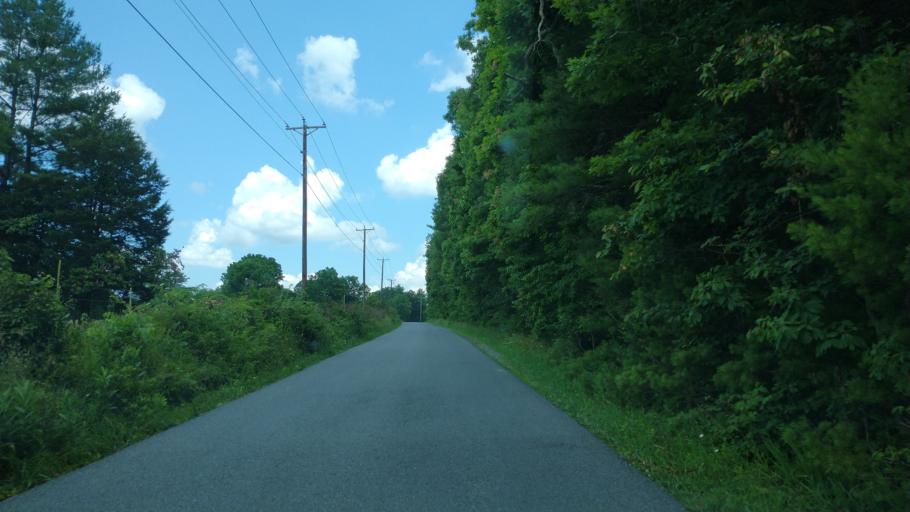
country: US
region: West Virginia
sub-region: Mercer County
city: Athens
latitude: 37.4575
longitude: -81.0399
